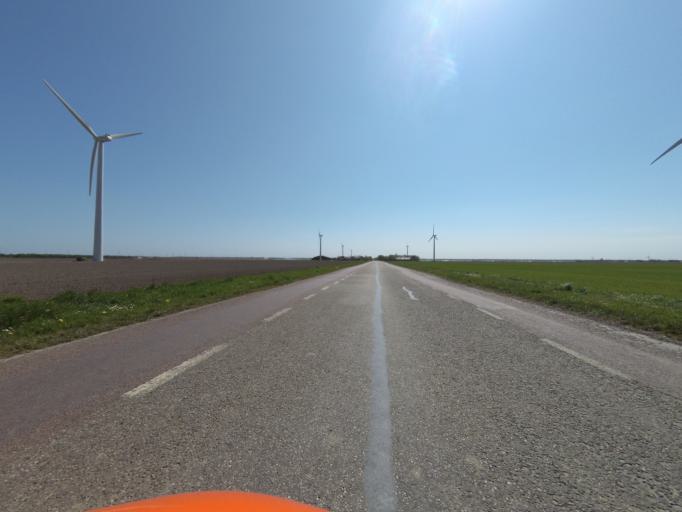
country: NL
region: Flevoland
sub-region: Gemeente Lelystad
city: Lelystad
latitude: 52.4140
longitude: 5.4113
